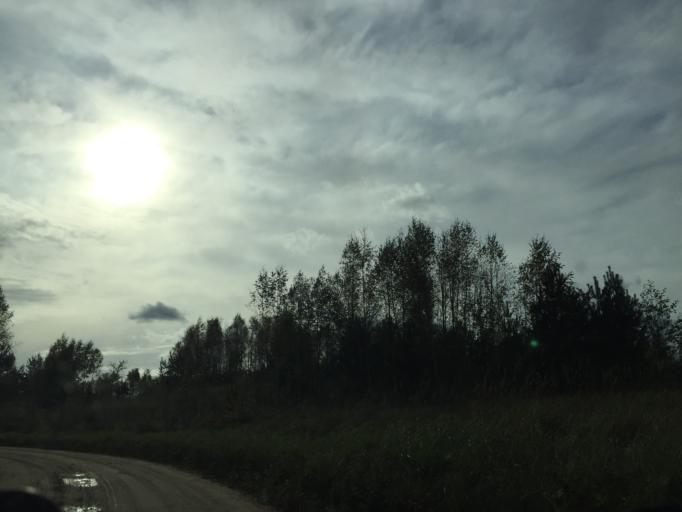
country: LV
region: Jaunpils
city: Jaunpils
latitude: 56.5779
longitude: 23.0237
